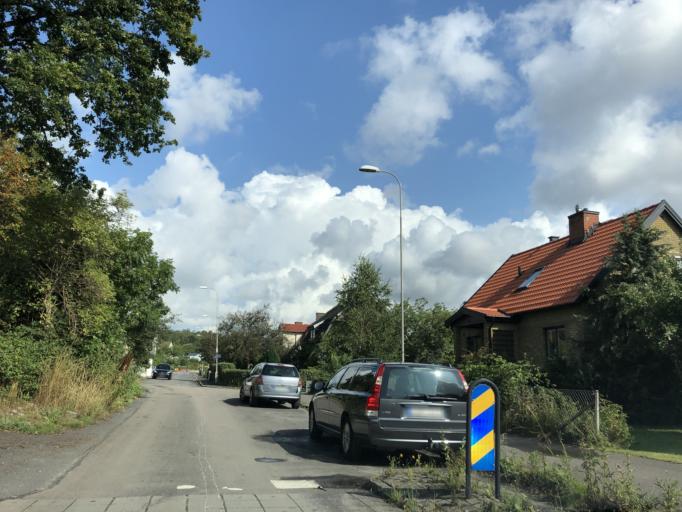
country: SE
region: Vaestra Goetaland
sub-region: Goteborg
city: Majorna
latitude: 57.7098
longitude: 11.9013
